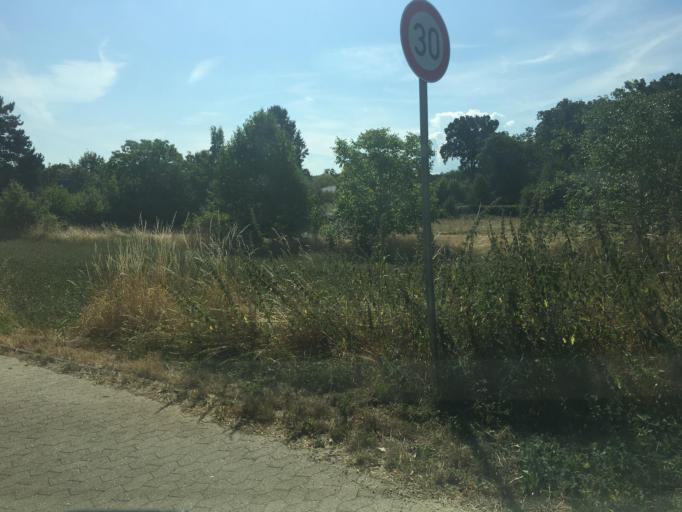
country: DE
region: North Rhine-Westphalia
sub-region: Regierungsbezirk Koln
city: Rheinbach
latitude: 50.6138
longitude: 6.9414
